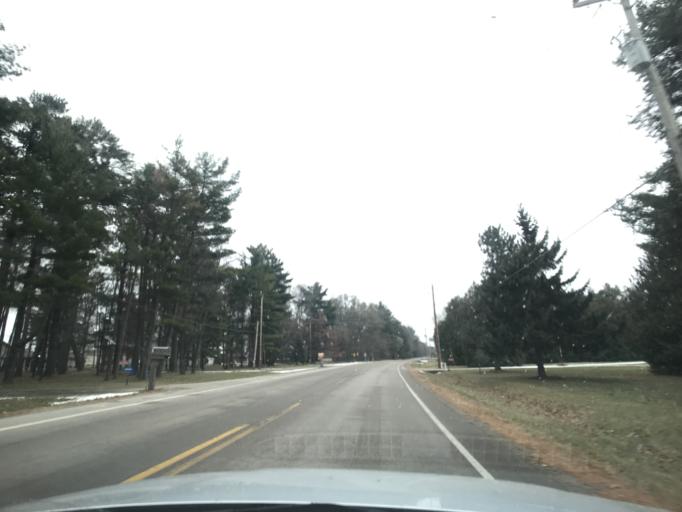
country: US
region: Wisconsin
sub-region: Marinette County
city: Marinette
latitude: 45.0633
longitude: -87.6194
